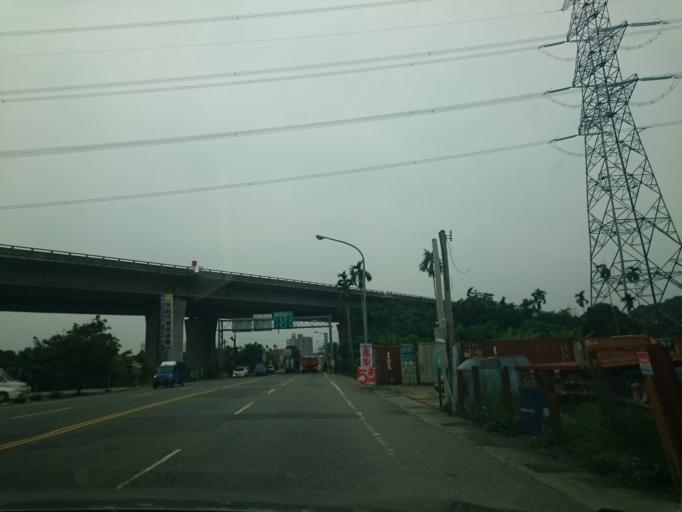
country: TW
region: Taiwan
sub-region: Nantou
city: Nantou
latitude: 23.8330
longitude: 120.7091
